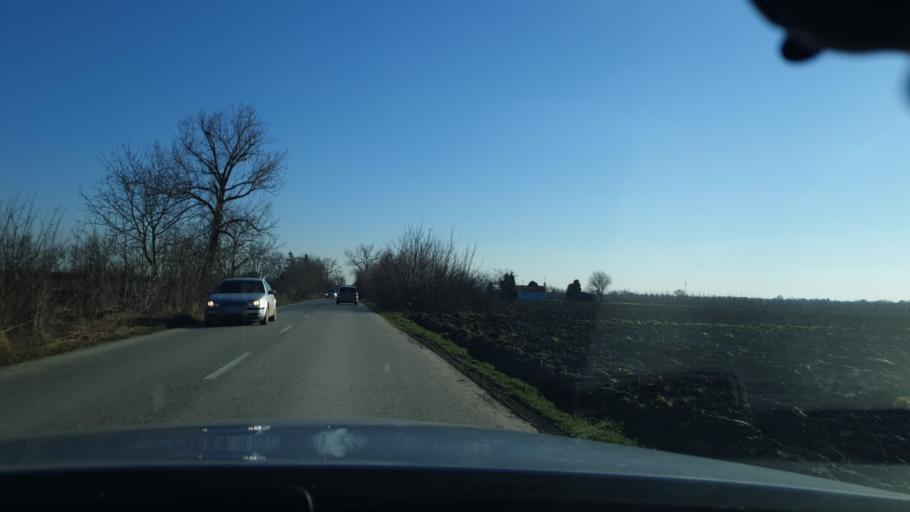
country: RS
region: Autonomna Pokrajina Vojvodina
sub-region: Sremski Okrug
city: Ruma
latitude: 45.0410
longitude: 19.8052
